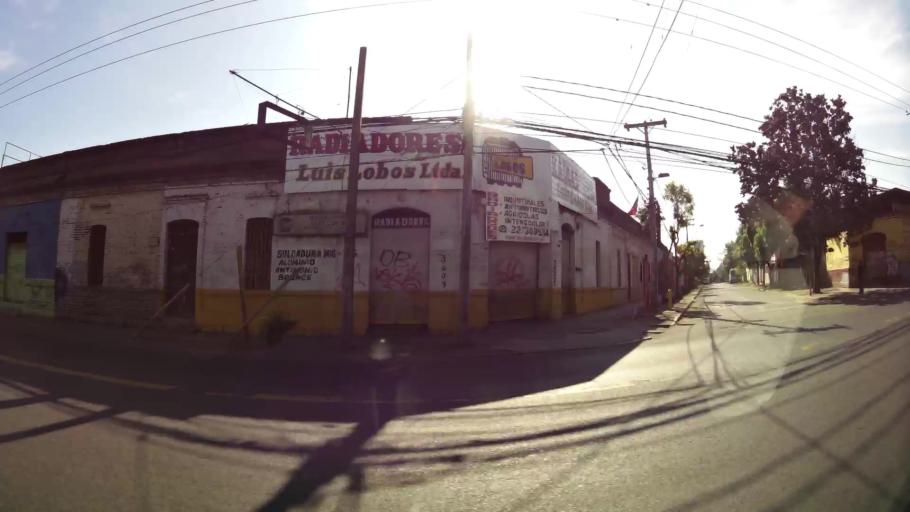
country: CL
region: Santiago Metropolitan
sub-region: Provincia de Santiago
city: Santiago
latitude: -33.3992
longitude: -70.6681
